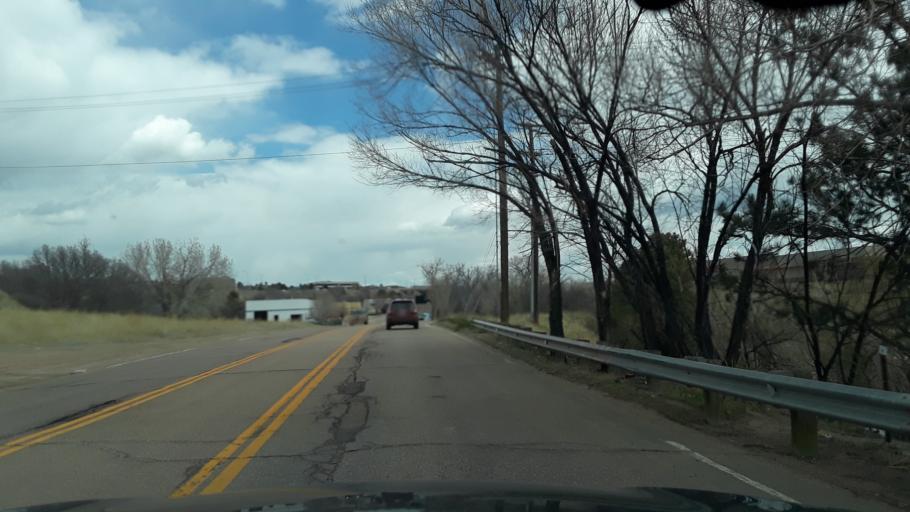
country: US
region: Colorado
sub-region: El Paso County
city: Colorado Springs
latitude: 38.9027
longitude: -104.8243
